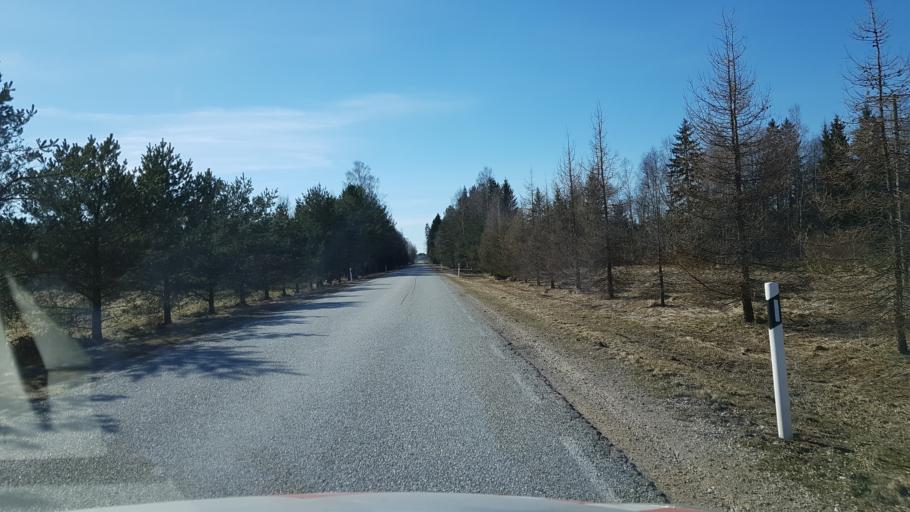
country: EE
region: Ida-Virumaa
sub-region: Kivioli linn
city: Kivioli
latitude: 59.2314
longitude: 26.7657
